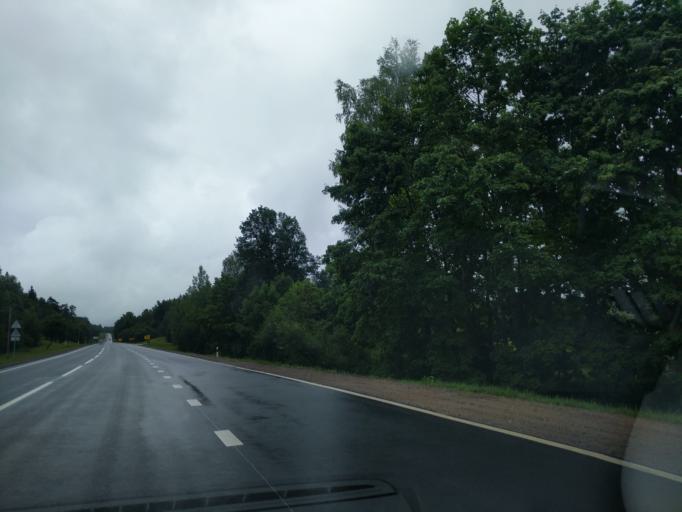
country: BY
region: Minsk
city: Syomkava
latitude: 54.2339
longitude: 27.4848
